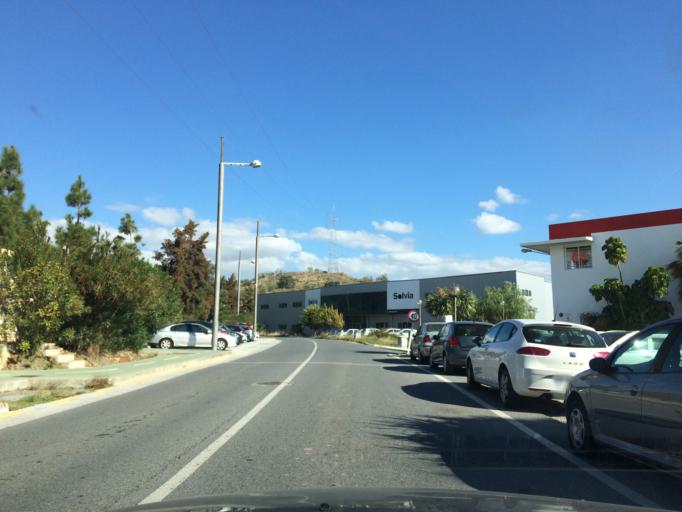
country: ES
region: Andalusia
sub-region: Provincia de Malaga
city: Estacion de Cartama
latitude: 36.7338
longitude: -4.5474
